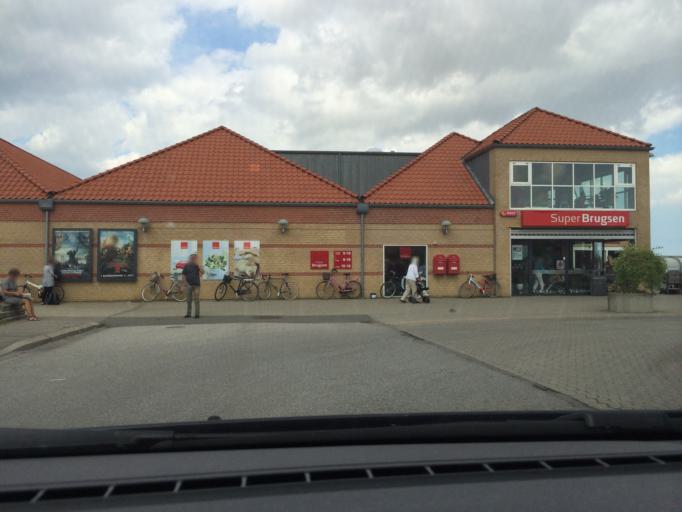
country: DK
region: Zealand
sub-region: Vordingborg Kommune
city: Stege
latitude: 54.9811
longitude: 12.2812
